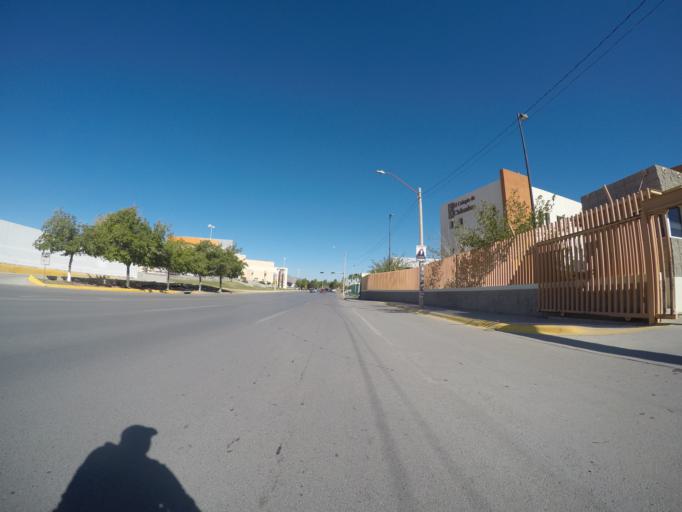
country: MX
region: Chihuahua
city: Ciudad Juarez
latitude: 31.7422
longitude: -106.4438
